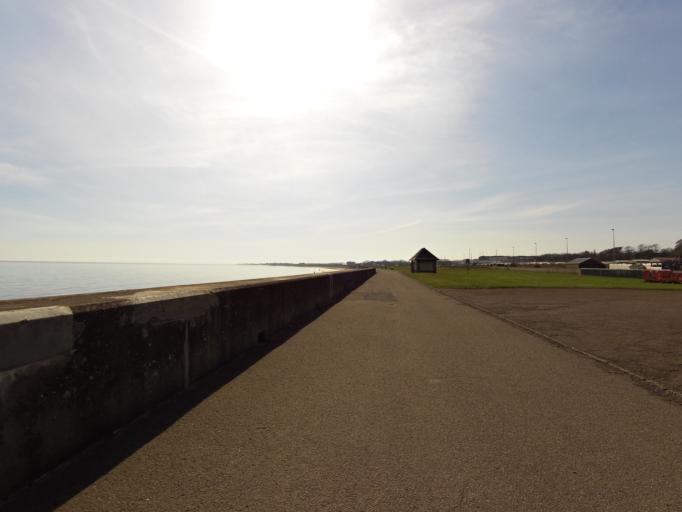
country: GB
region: Scotland
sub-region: Angus
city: Arbroath
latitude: 56.5511
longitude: -2.6043
